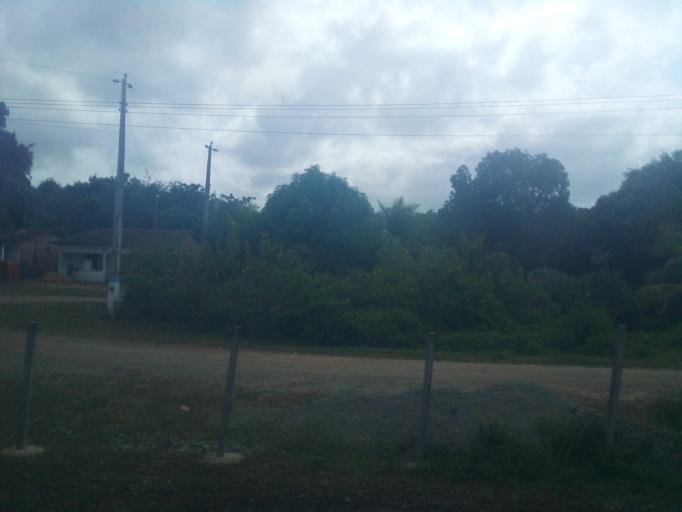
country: BR
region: Maranhao
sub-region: Anajatuba
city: Anajatuba
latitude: -3.0357
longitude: -44.3472
